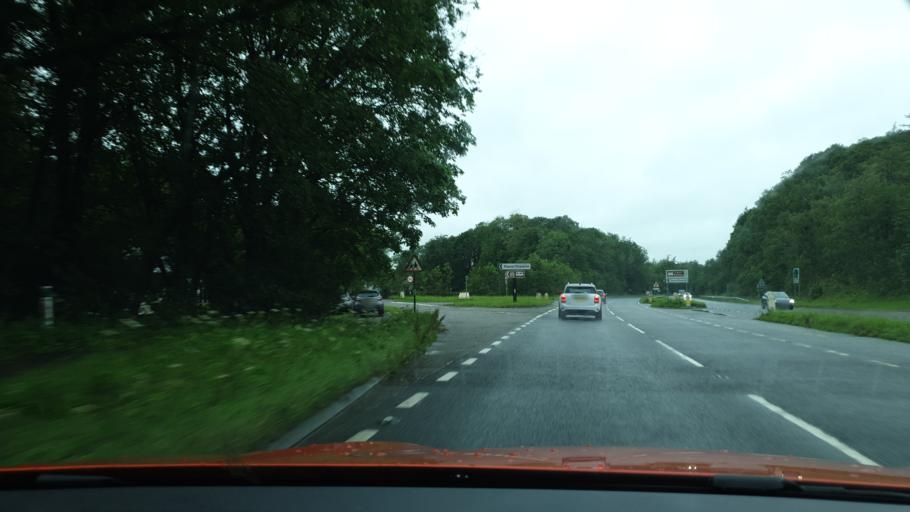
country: GB
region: England
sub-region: Cumbria
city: Grange-over-Sands
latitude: 54.2492
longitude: -2.9994
